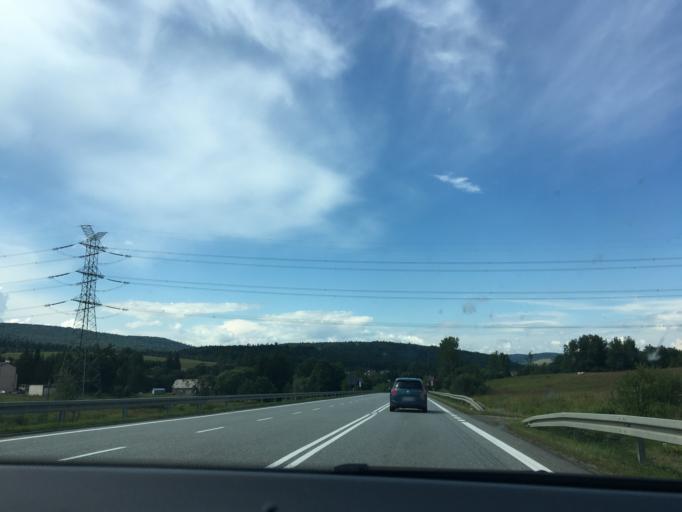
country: PL
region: Subcarpathian Voivodeship
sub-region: Powiat krosnienski
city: Jasliska
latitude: 49.4267
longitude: 21.6907
